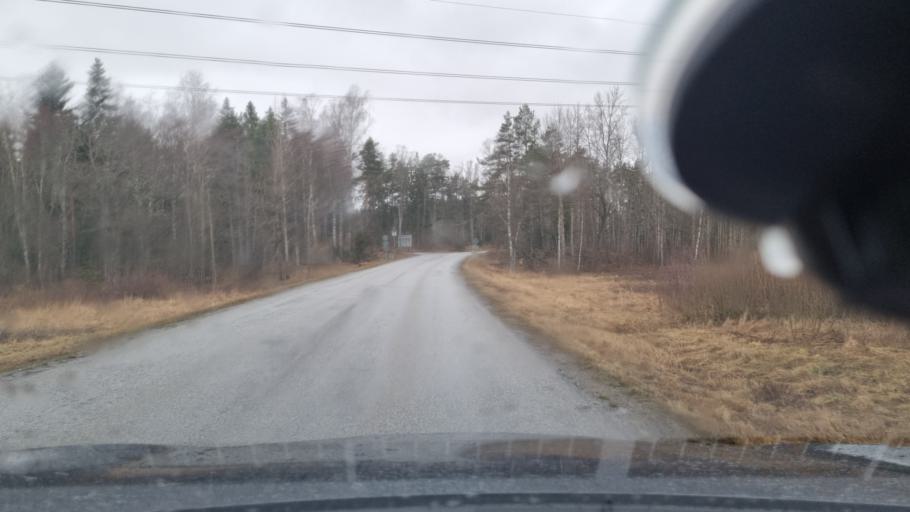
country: SE
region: Stockholm
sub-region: Sigtuna Kommun
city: Sigtuna
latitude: 59.5667
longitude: 17.6889
